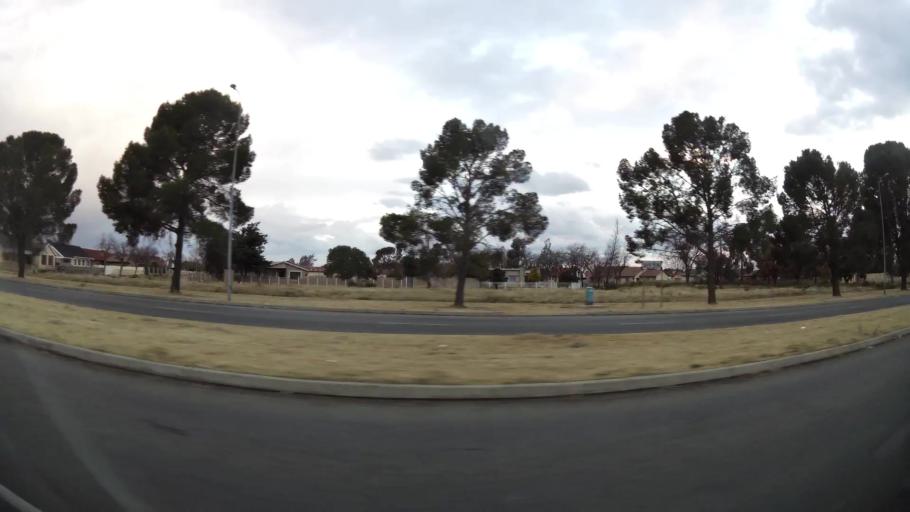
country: ZA
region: Orange Free State
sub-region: Lejweleputswa District Municipality
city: Welkom
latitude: -27.9686
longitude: 26.7647
